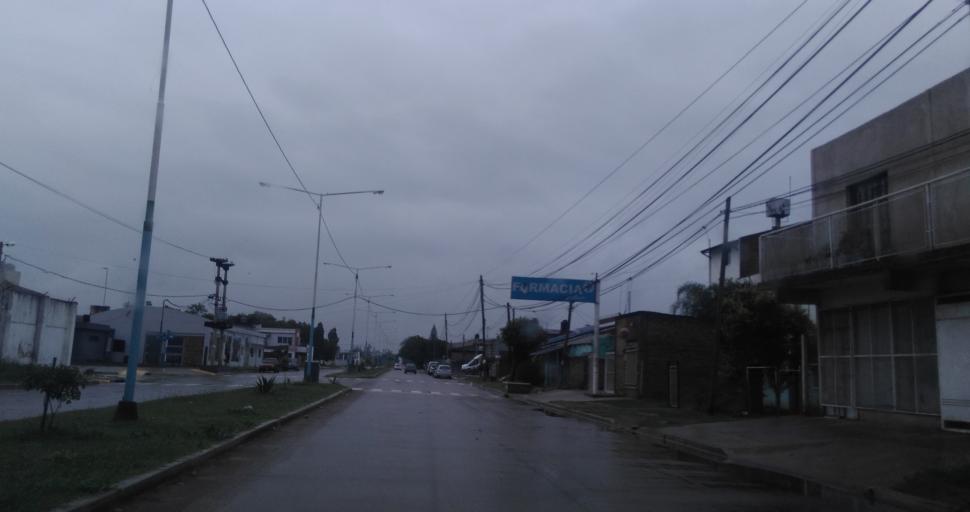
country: AR
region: Chaco
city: Fontana
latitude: -27.4156
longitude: -59.0346
